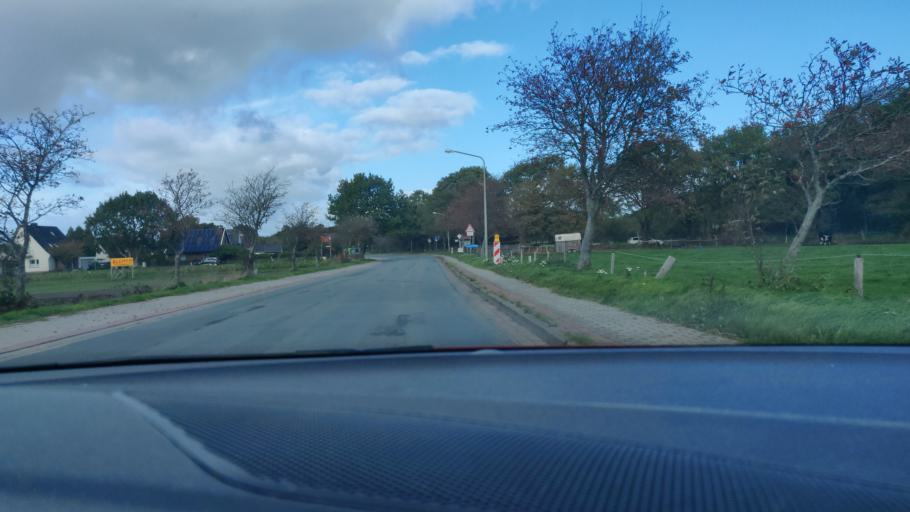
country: DE
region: Lower Saxony
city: Cuxhaven
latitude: 53.8563
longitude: 8.6385
